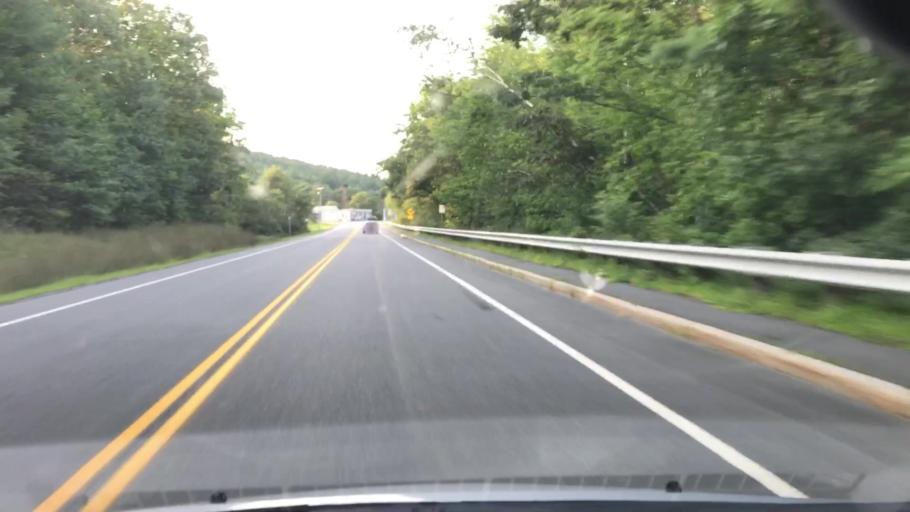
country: US
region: New Hampshire
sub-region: Grafton County
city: Rumney
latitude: 43.9234
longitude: -71.8903
